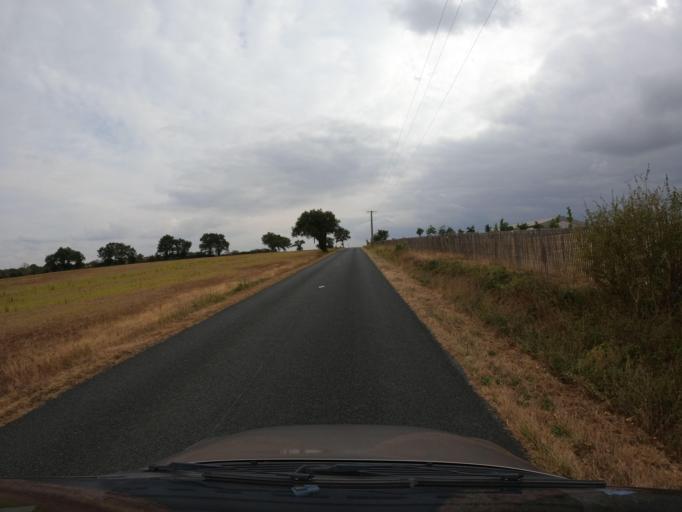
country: FR
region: Pays de la Loire
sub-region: Departement de la Vendee
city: Les Landes-Genusson
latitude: 46.9880
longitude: -1.1102
